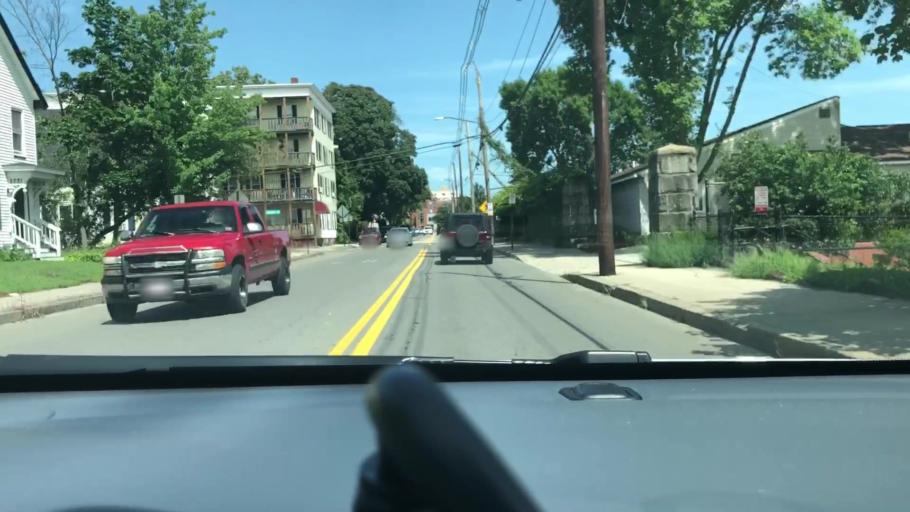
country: US
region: New Hampshire
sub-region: Hillsborough County
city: Manchester
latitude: 42.9874
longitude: -71.4740
